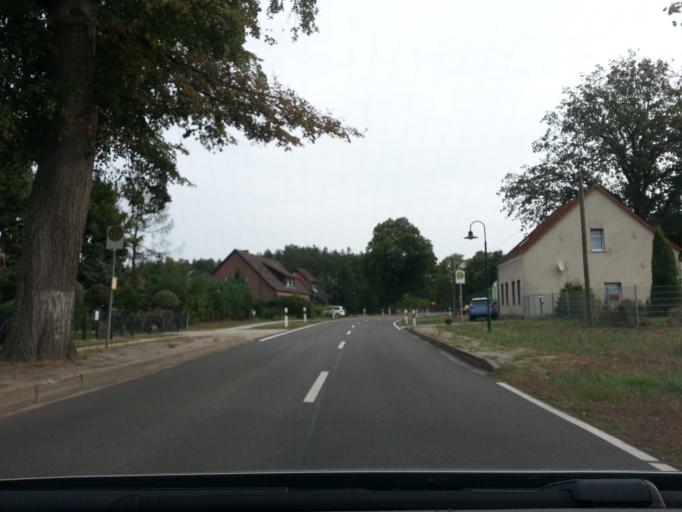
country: DE
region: Mecklenburg-Vorpommern
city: Ferdinandshof
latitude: 53.7077
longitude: 13.9439
